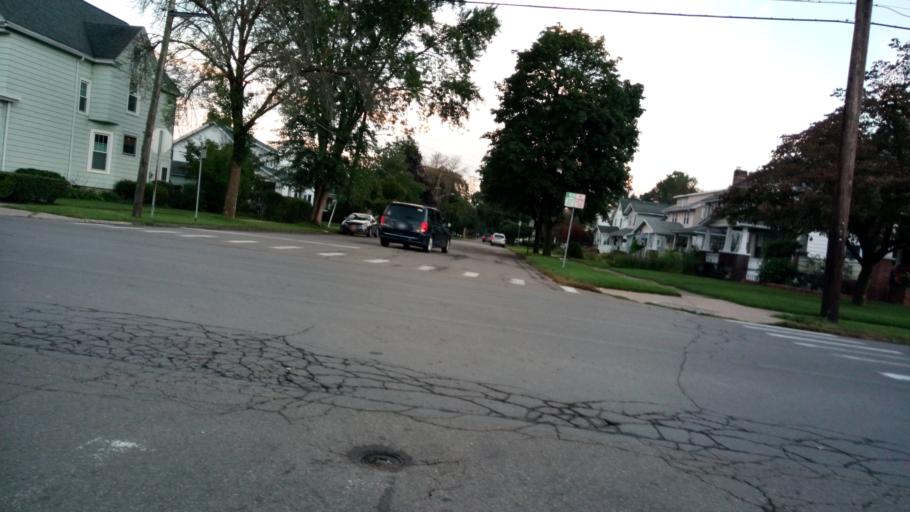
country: US
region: New York
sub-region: Chemung County
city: Elmira
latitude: 42.0993
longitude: -76.8268
